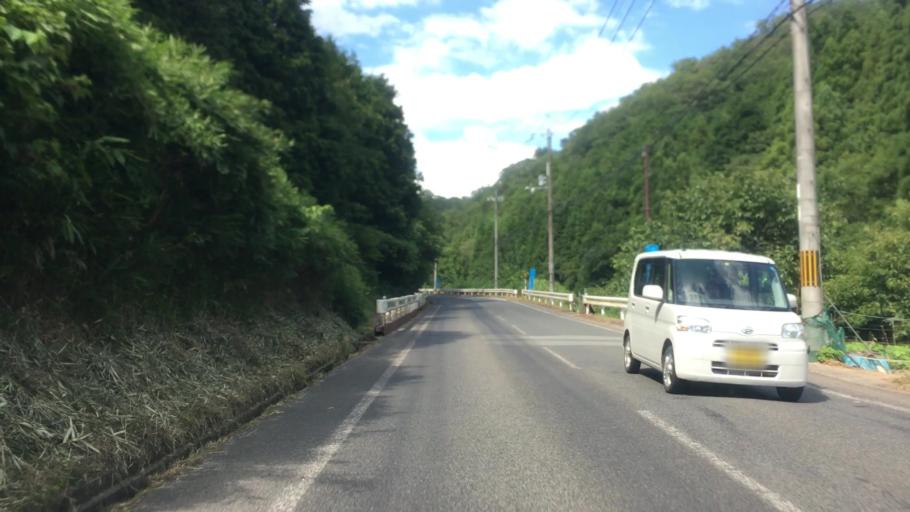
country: JP
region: Hyogo
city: Toyooka
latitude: 35.5076
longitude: 134.7780
